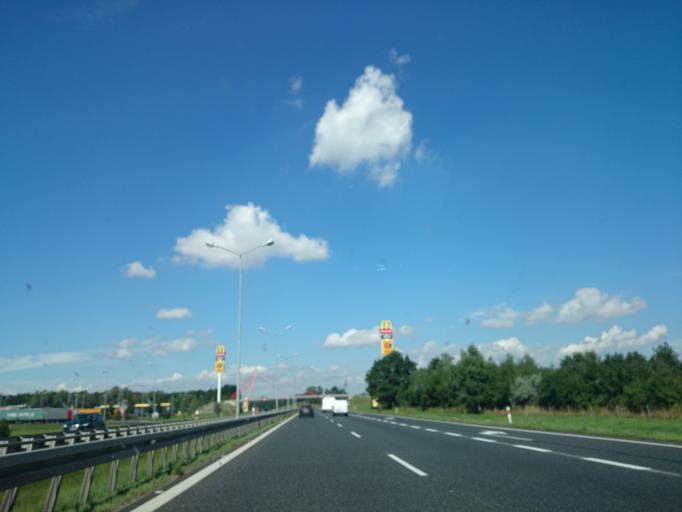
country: PL
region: Lower Silesian Voivodeship
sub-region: Powiat strzelinski
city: Wiazow
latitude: 50.8435
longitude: 17.2575
